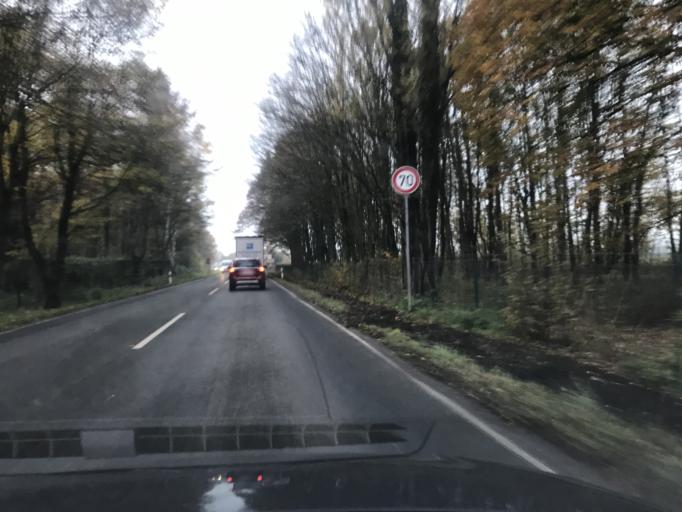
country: DE
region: North Rhine-Westphalia
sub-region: Regierungsbezirk Arnsberg
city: Welver
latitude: 51.6827
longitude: 7.9740
